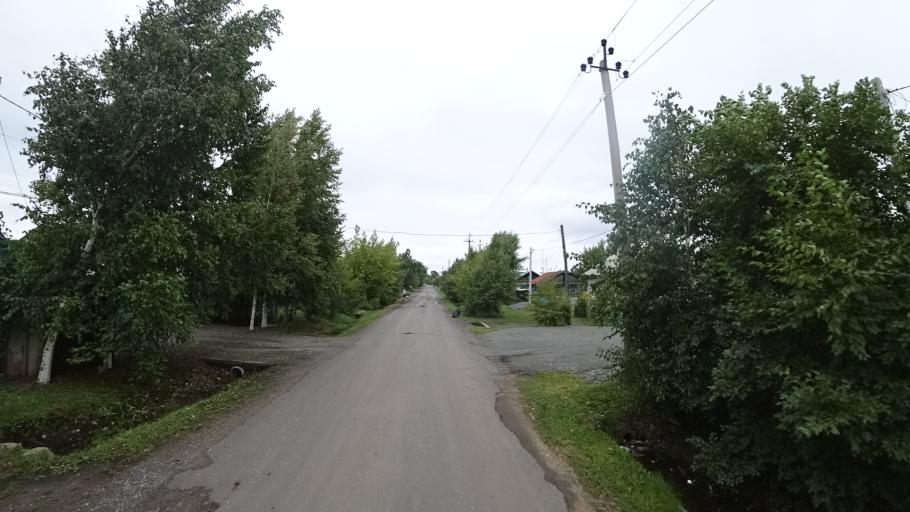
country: RU
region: Primorskiy
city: Chernigovka
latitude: 44.3410
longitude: 132.5878
